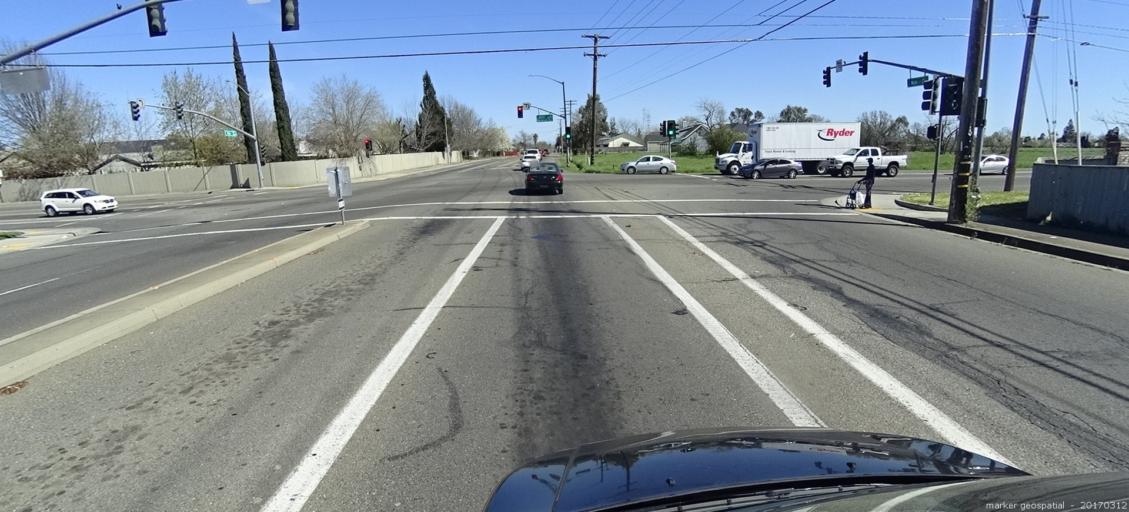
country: US
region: California
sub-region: Sacramento County
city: Rio Linda
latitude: 38.6549
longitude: -121.4574
